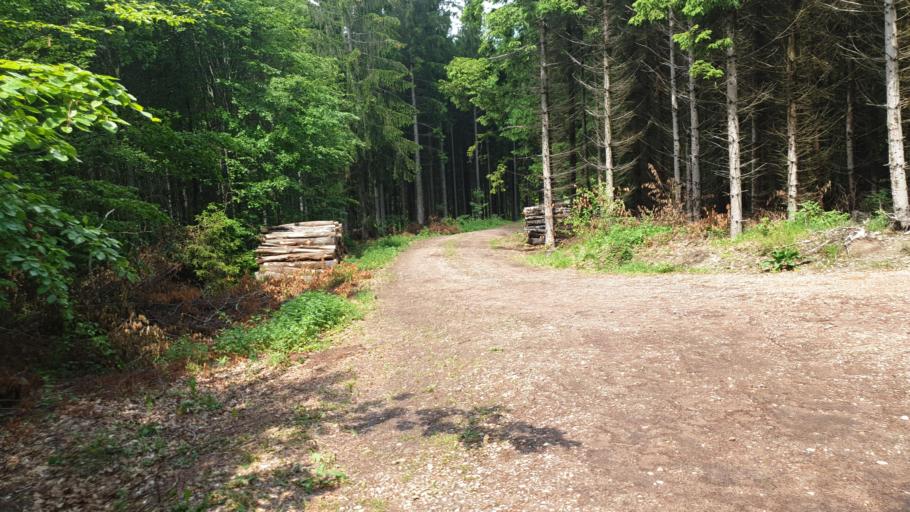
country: DE
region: Saxony
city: Gornau
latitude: 50.7868
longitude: 12.9770
